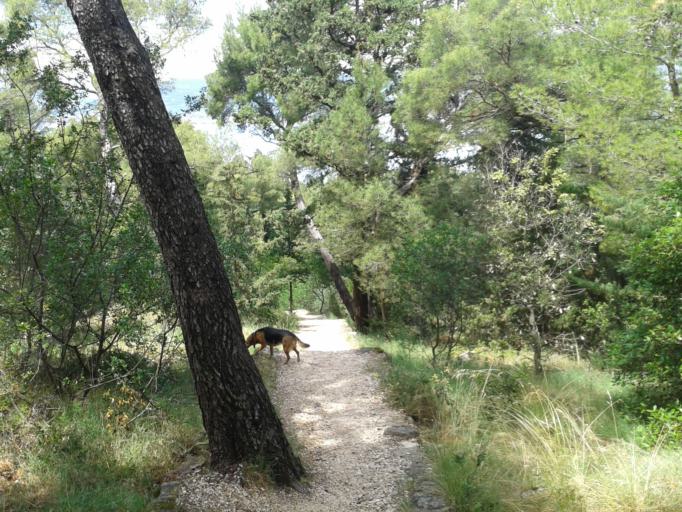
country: HR
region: Splitsko-Dalmatinska
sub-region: Grad Split
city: Split
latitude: 43.5106
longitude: 16.4212
